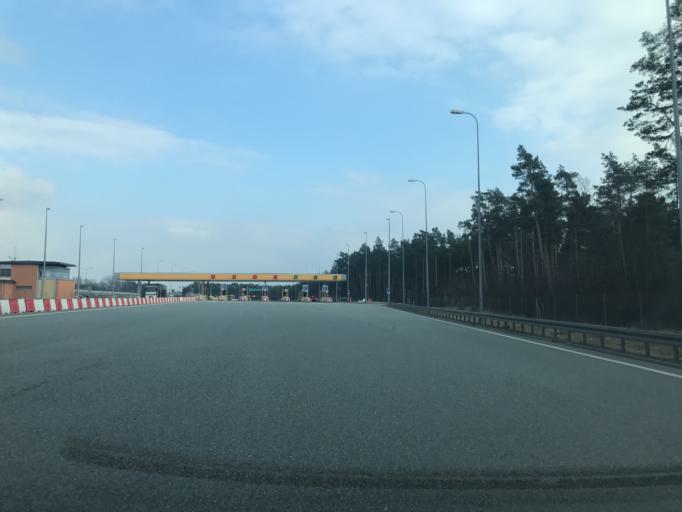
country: PL
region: Kujawsko-Pomorskie
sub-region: Powiat torunski
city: Lubicz Dolny
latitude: 53.0361
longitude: 18.7354
